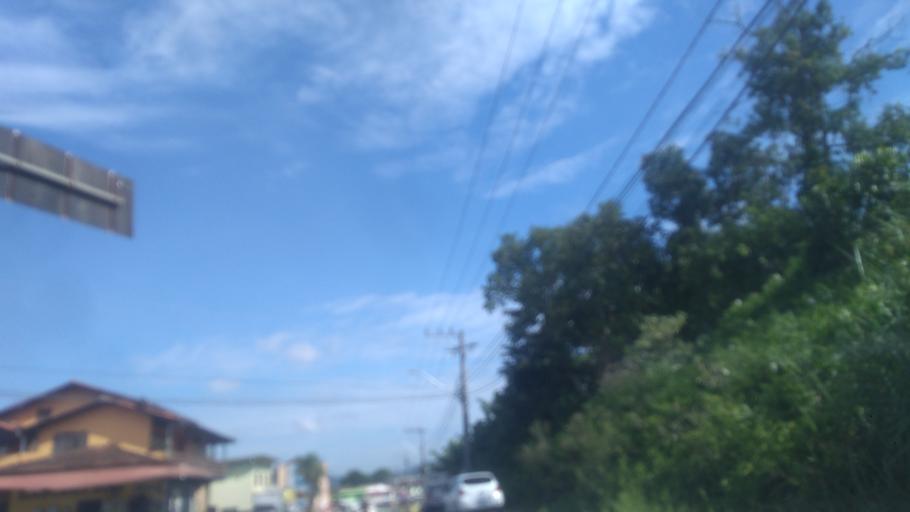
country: BR
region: Santa Catarina
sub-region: Joinville
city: Joinville
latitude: -26.3270
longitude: -48.8068
